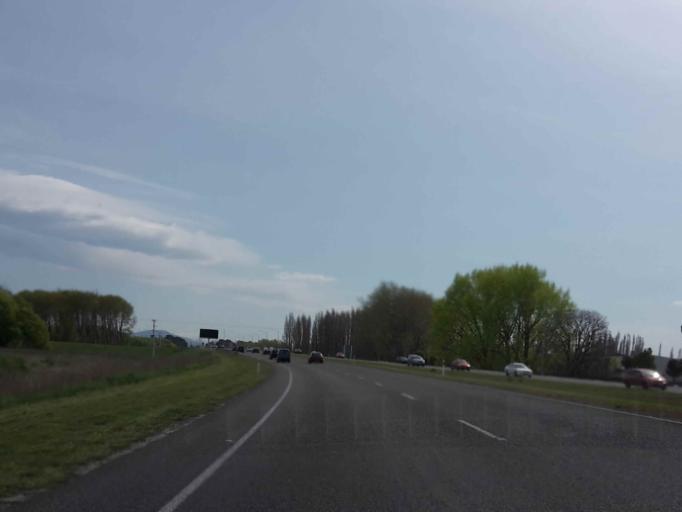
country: NZ
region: Canterbury
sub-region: Waimakariri District
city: Kaiapoi
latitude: -43.4222
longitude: 172.6484
